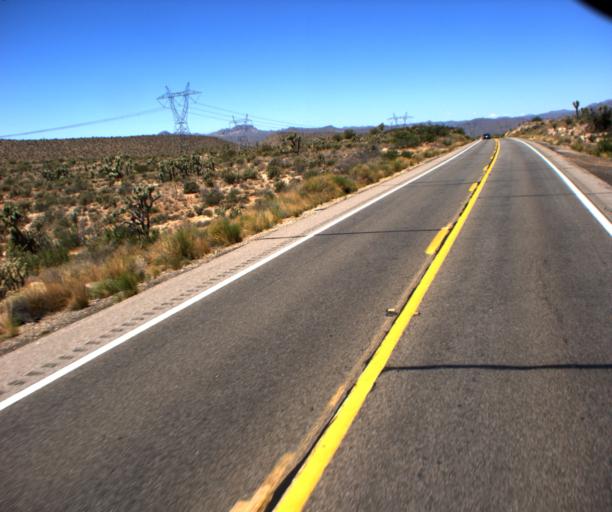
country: US
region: Arizona
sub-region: Yavapai County
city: Bagdad
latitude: 34.3327
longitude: -113.1447
